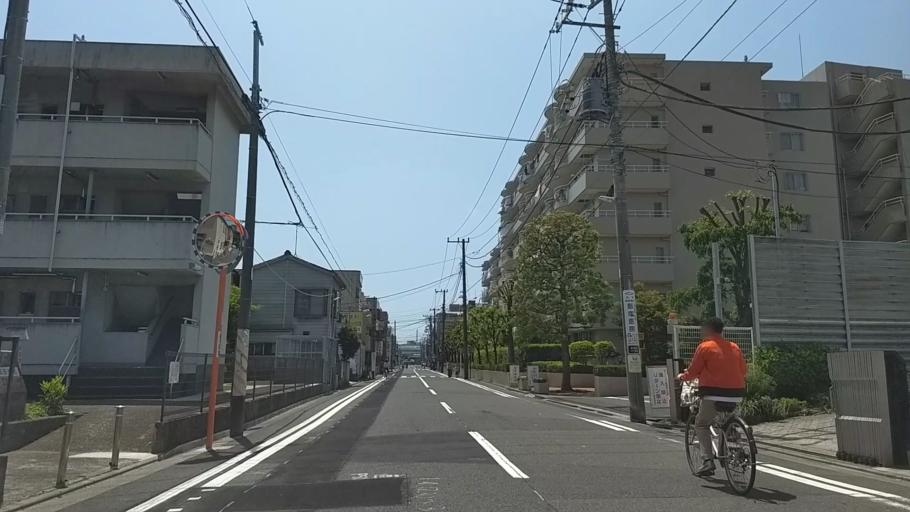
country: JP
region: Kanagawa
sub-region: Kawasaki-shi
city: Kawasaki
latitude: 35.5064
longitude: 139.6985
